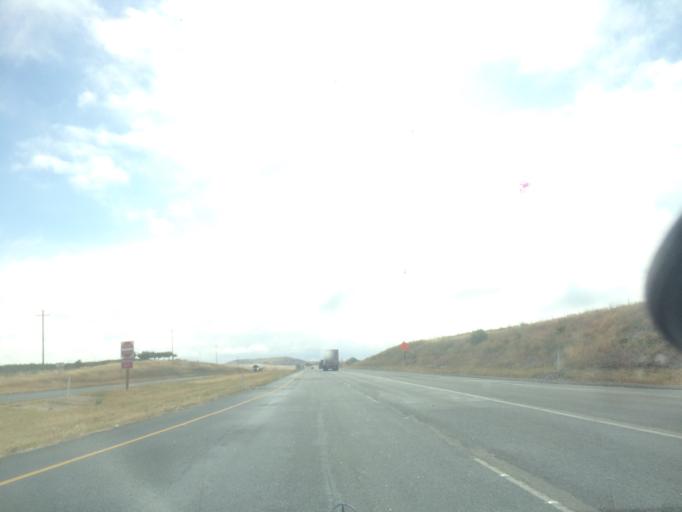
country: US
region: California
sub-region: San Luis Obispo County
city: Paso Robles
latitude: 35.6593
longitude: -120.5609
